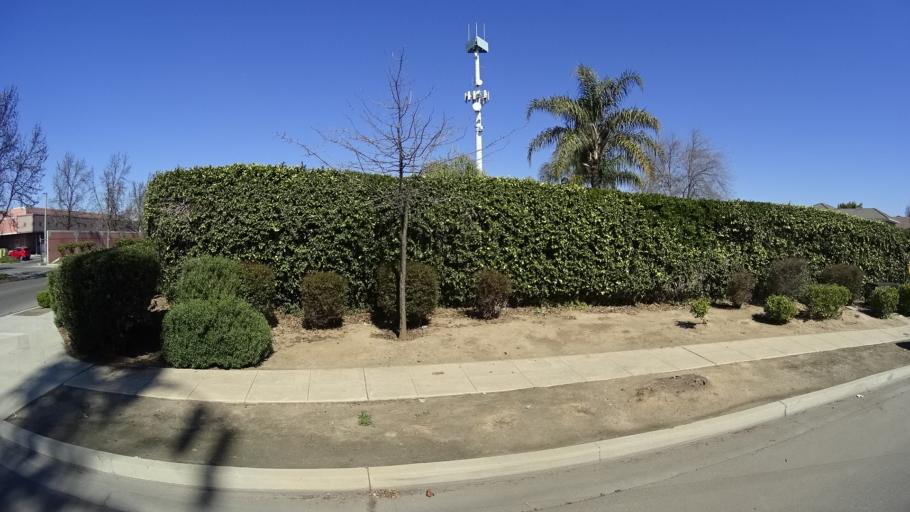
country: US
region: California
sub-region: Fresno County
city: Clovis
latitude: 36.8504
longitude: -119.7701
